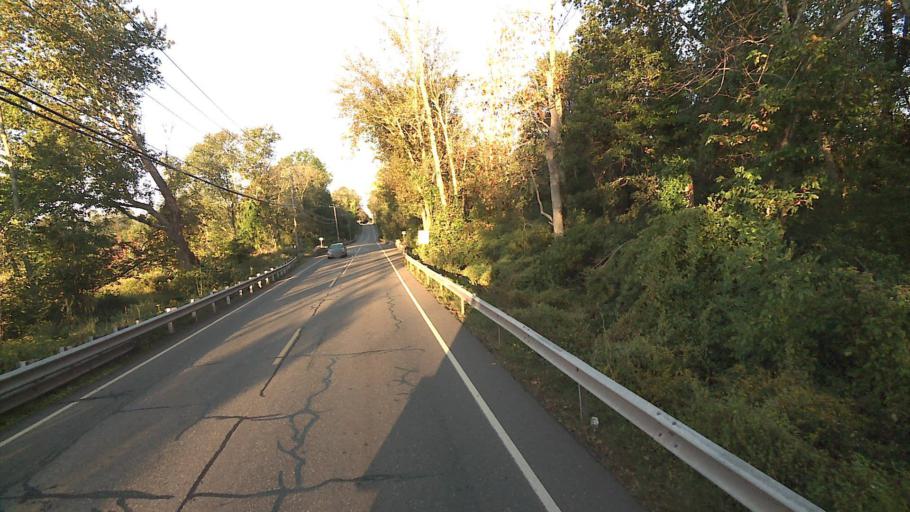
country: US
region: Connecticut
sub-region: Middlesex County
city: Durham
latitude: 41.4774
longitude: -72.6878
